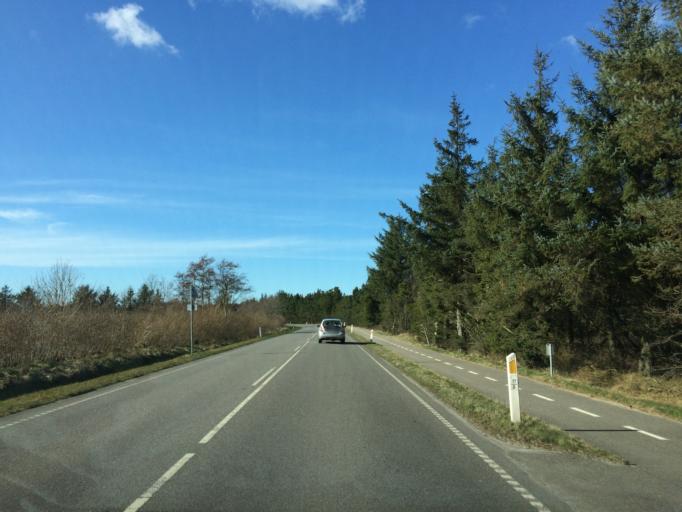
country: DK
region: South Denmark
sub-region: Varde Kommune
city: Oksbol
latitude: 55.7232
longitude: 8.2853
